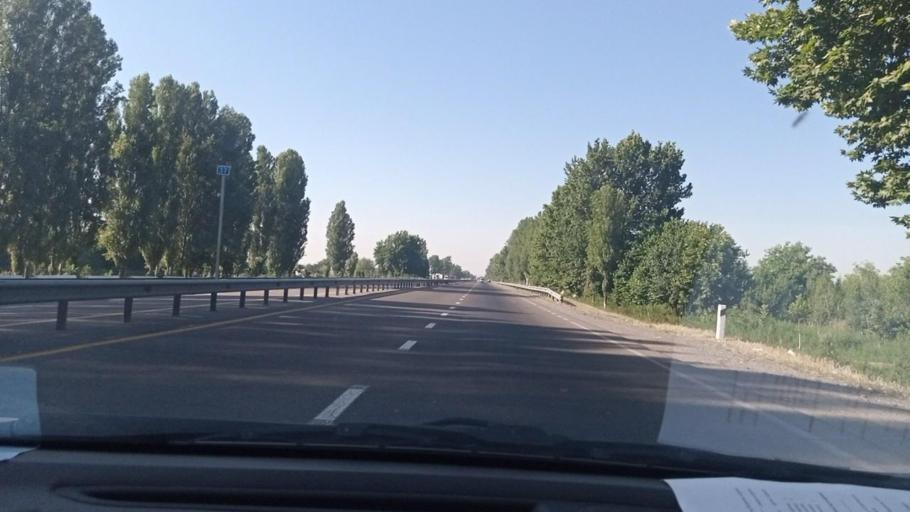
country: UZ
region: Toshkent Shahri
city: Bektemir
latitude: 41.2127
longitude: 69.4026
